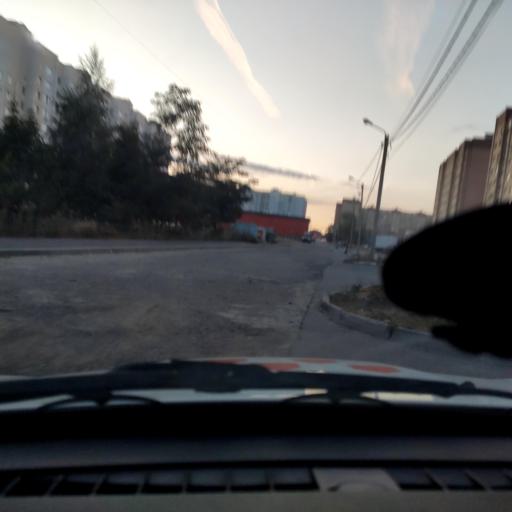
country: RU
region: Voronezj
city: Shilovo
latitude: 51.5602
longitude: 39.1180
